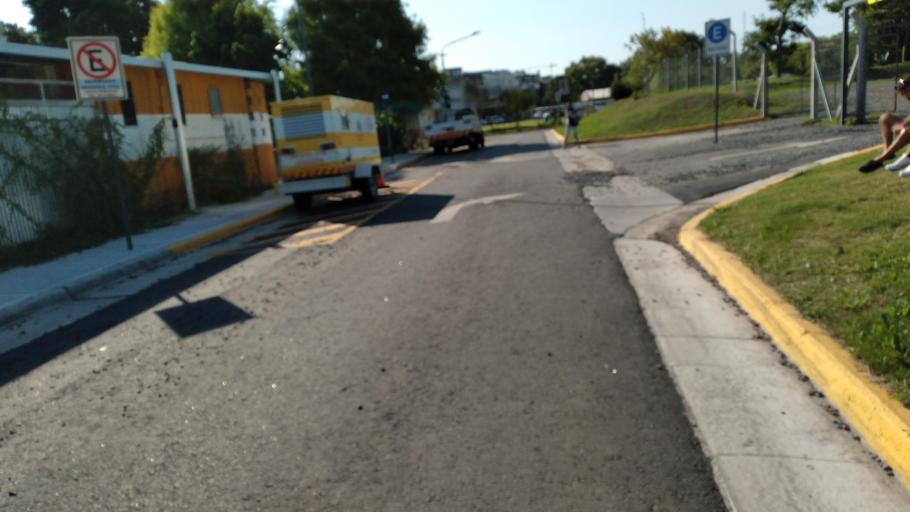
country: AR
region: Buenos Aires
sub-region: Partido de Vicente Lopez
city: Olivos
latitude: -34.5004
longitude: -58.4787
